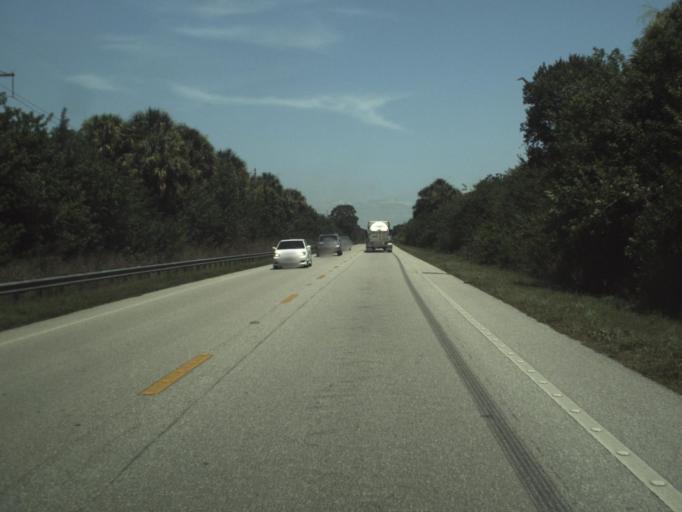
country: US
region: Florida
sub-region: Martin County
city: Indiantown
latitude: 27.1116
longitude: -80.6058
